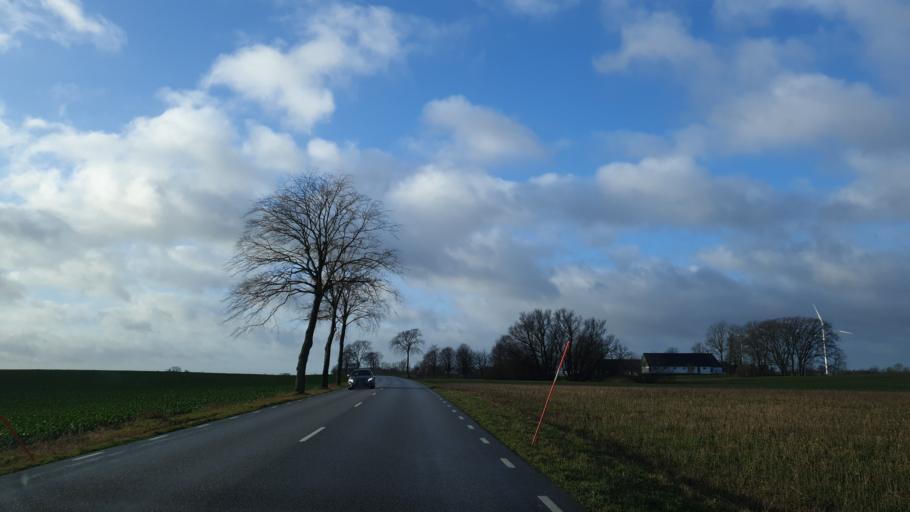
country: SE
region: Skane
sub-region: Trelleborgs Kommun
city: Anderslov
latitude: 55.4245
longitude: 13.4234
